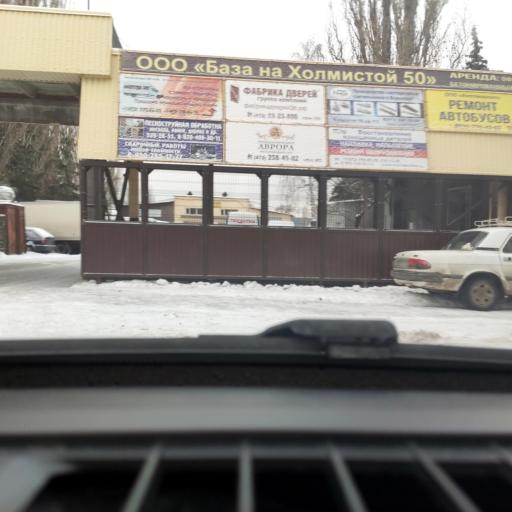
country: RU
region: Voronezj
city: Voronezh
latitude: 51.6694
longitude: 39.1388
